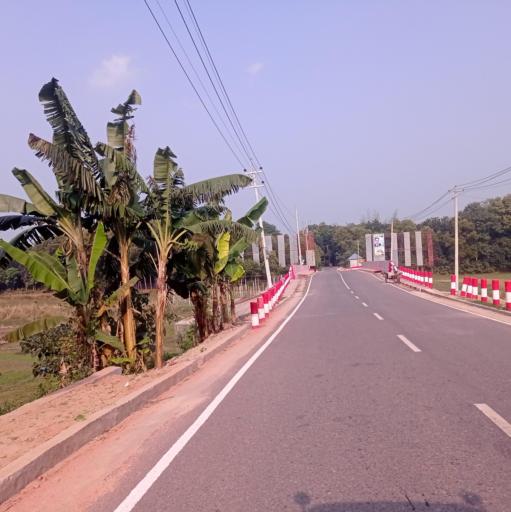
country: BD
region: Dhaka
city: Bhairab Bazar
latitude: 24.0544
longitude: 90.8353
